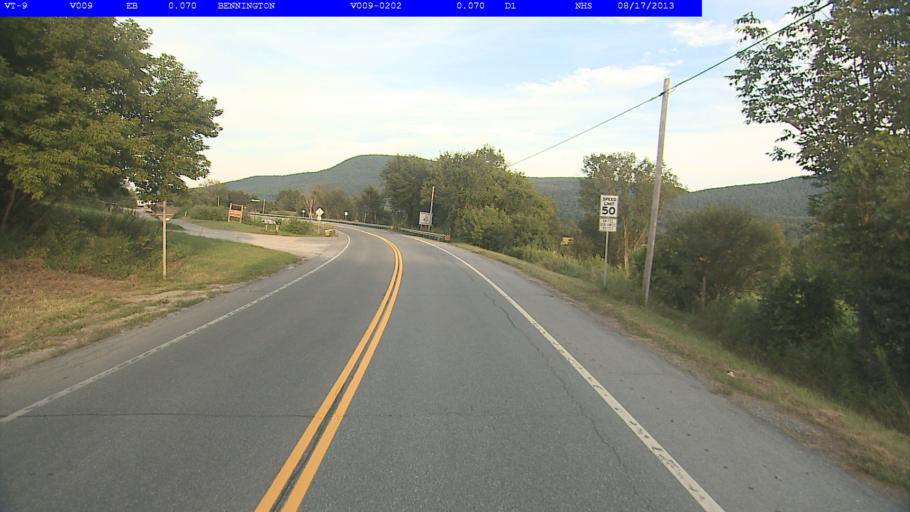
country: US
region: Vermont
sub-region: Bennington County
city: North Bennington
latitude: 42.8735
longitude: -73.2758
